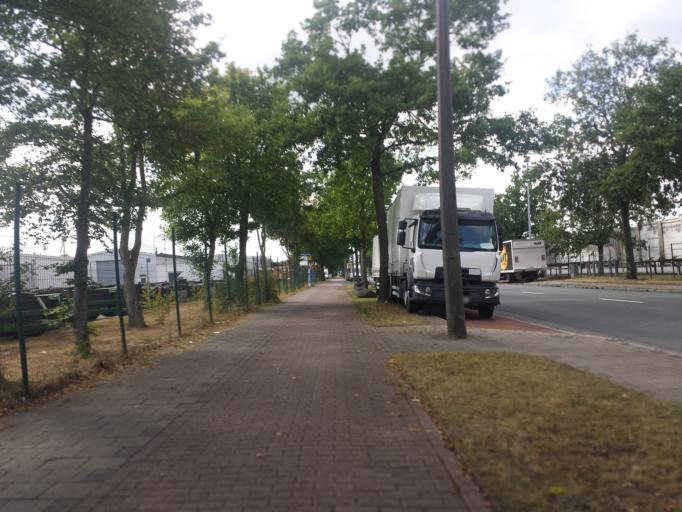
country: DE
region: Lower Saxony
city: Stuhr
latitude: 53.0835
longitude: 8.7236
